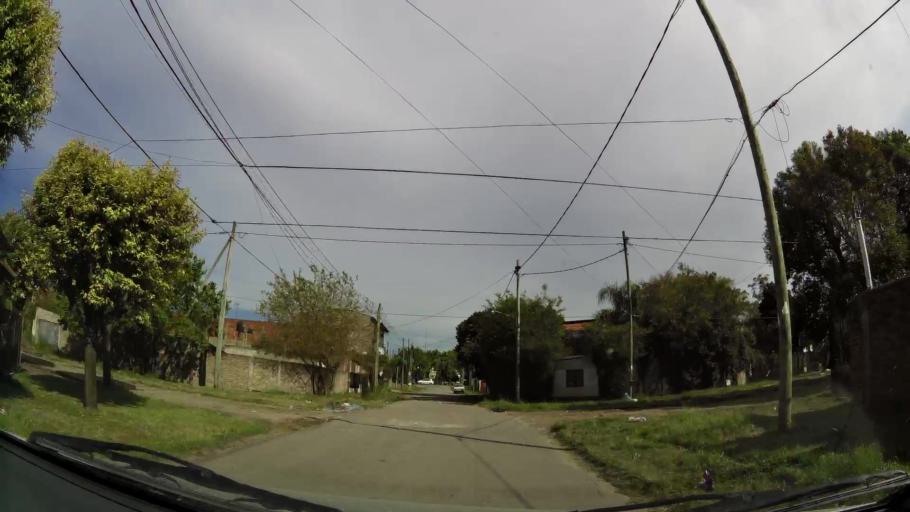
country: AR
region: Buenos Aires
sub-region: Partido de Almirante Brown
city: Adrogue
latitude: -34.8161
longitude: -58.3539
